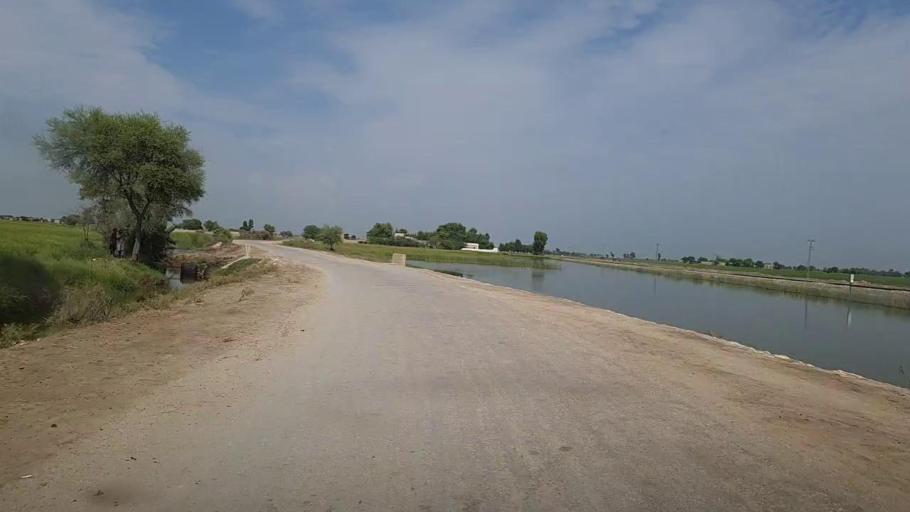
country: PK
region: Sindh
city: Thul
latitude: 28.2587
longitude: 68.8108
